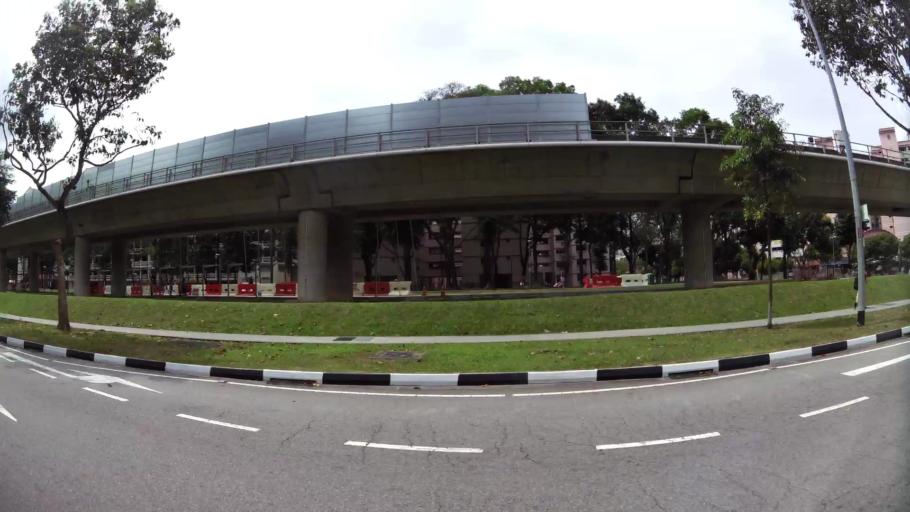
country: MY
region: Johor
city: Johor Bahru
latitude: 1.4002
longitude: 103.7484
